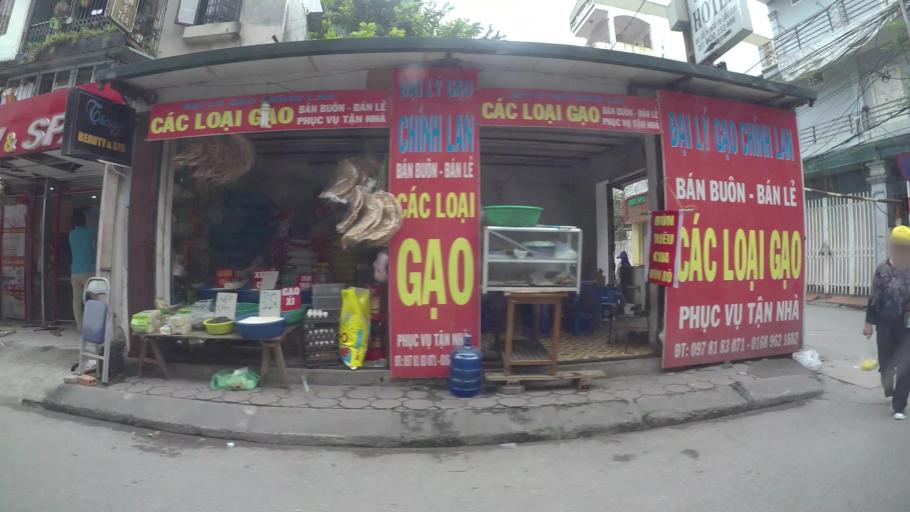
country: VN
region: Ha Noi
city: Cau Giay
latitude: 21.0340
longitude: 105.8172
